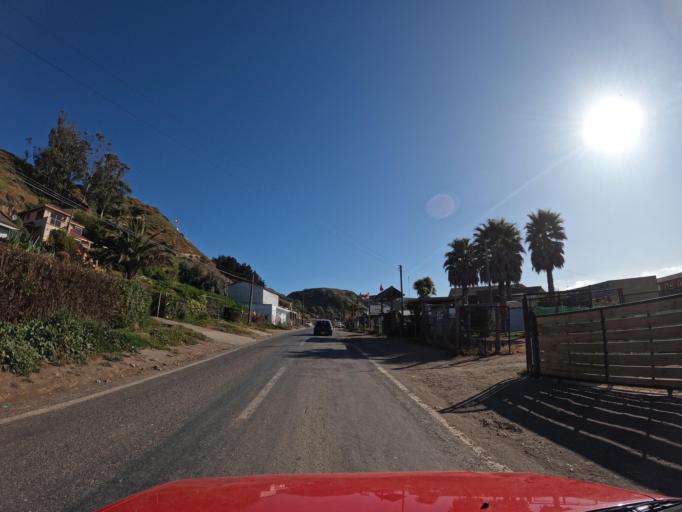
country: CL
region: Maule
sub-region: Provincia de Talca
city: Constitucion
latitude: -34.8829
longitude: -72.1582
